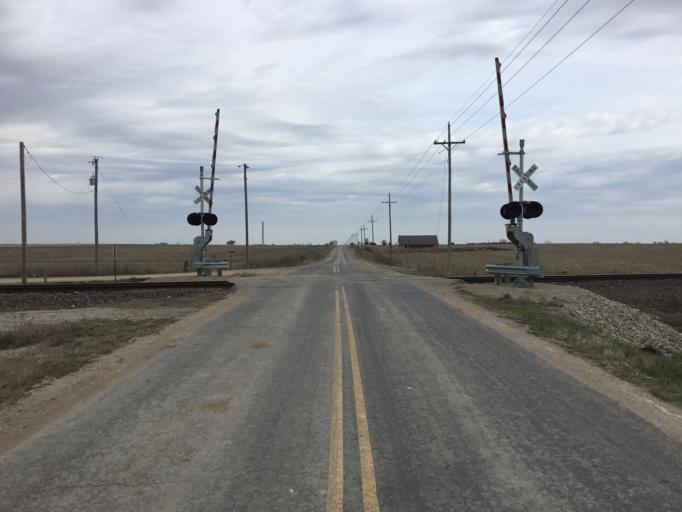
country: US
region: Kansas
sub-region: Russell County
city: Russell
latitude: 38.8860
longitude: -99.0025
